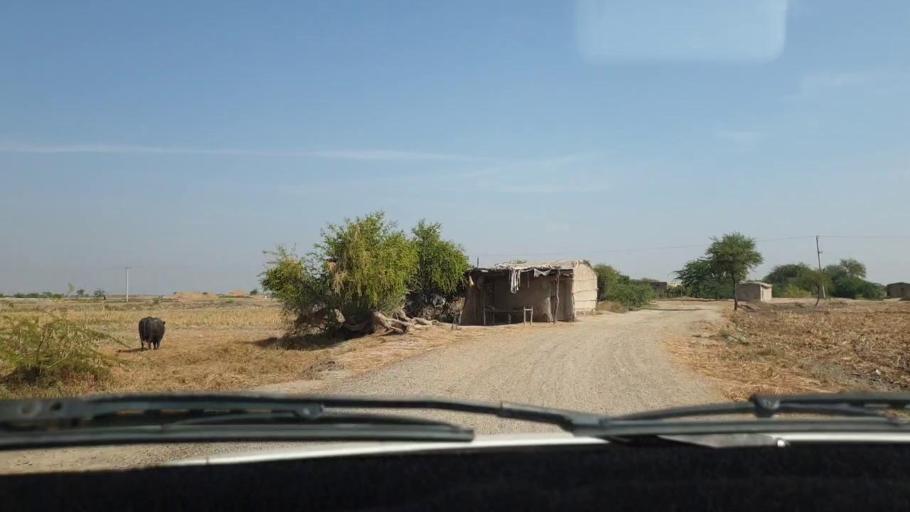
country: PK
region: Sindh
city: Bulri
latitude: 24.8627
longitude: 68.4741
